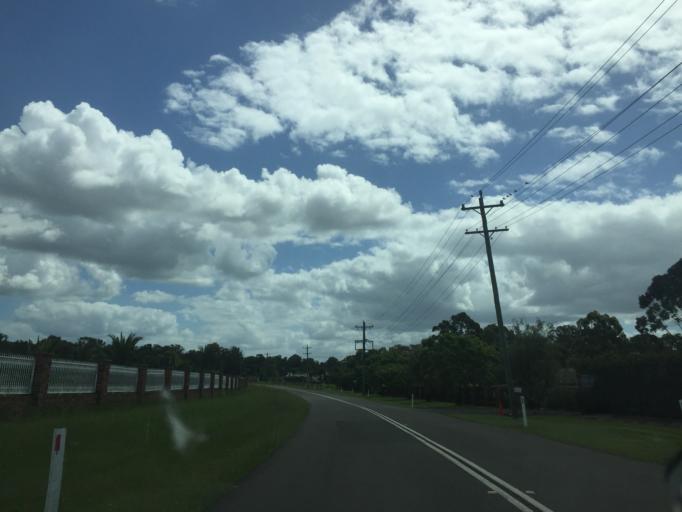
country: AU
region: New South Wales
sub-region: Penrith Municipality
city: Kingswood Park
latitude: -33.7978
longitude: 150.7409
